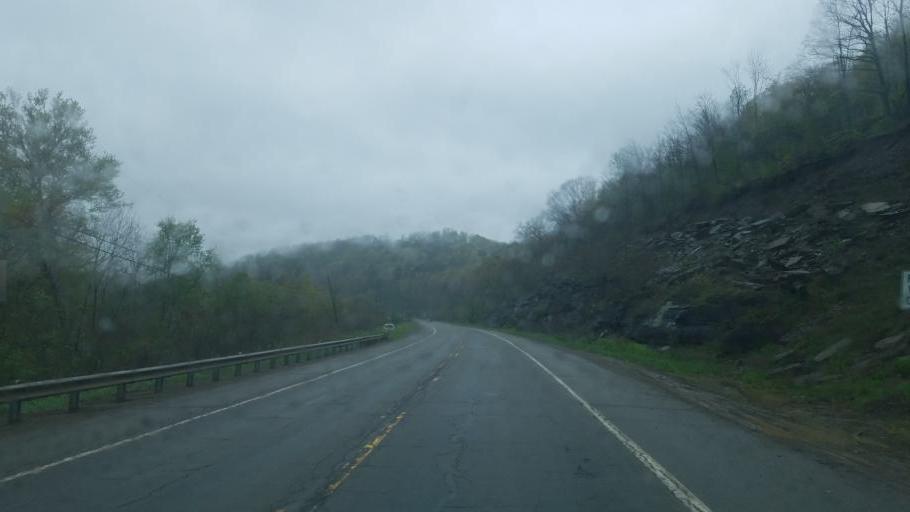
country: US
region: Pennsylvania
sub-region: McKean County
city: Port Allegany
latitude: 41.7918
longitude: -78.1846
